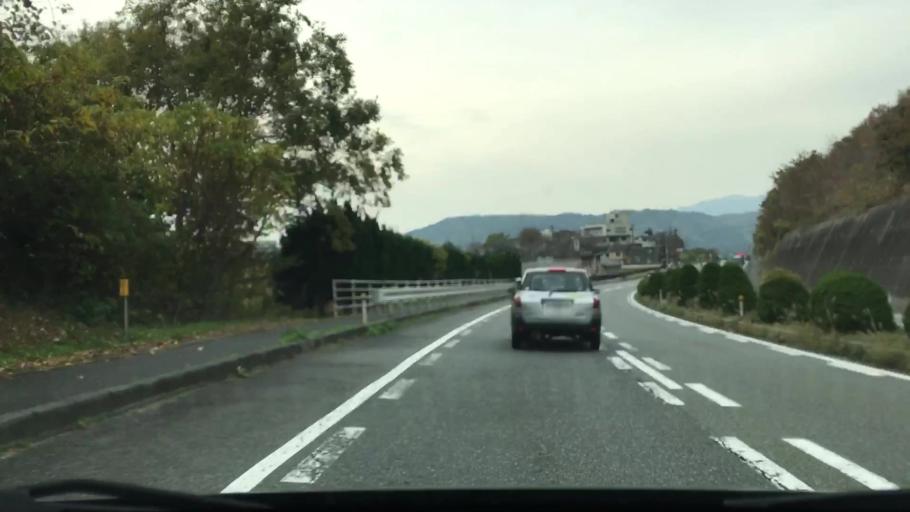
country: JP
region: Yamaguchi
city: Tokuyama
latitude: 34.0742
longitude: 131.7487
